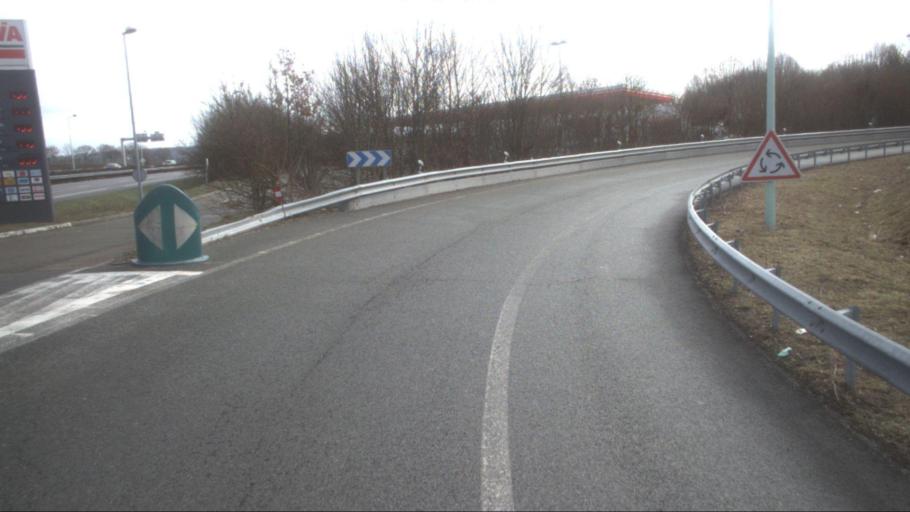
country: FR
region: Ile-de-France
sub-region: Departement des Yvelines
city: Houdan
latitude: 48.7919
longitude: 1.6331
